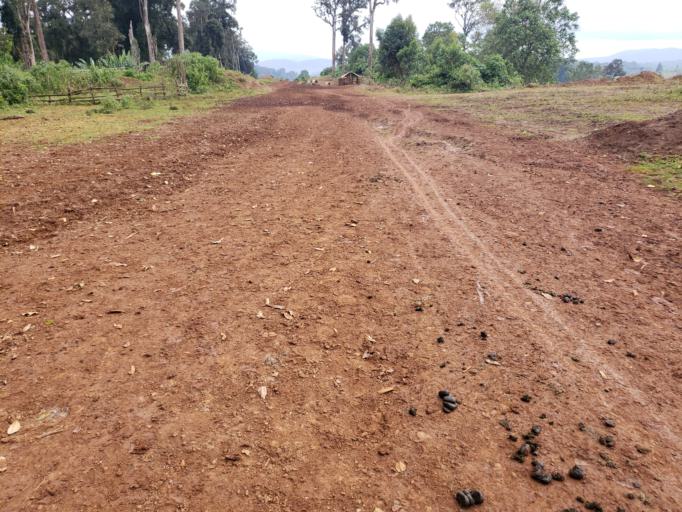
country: ET
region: Oromiya
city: Dodola
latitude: 6.5525
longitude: 39.4226
